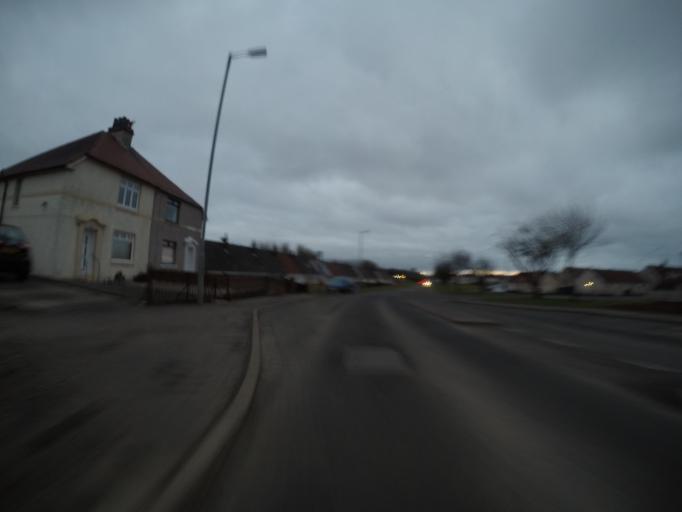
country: GB
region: Scotland
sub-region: North Ayrshire
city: Kilwinning
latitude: 55.6511
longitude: -4.6993
